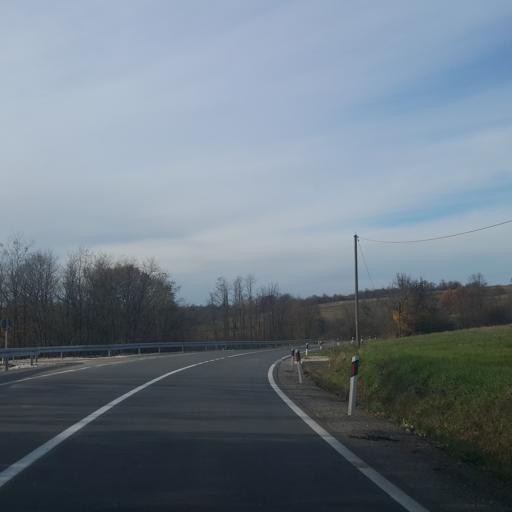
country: RS
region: Central Serbia
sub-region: Sumadijski Okrug
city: Arangelovac
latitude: 44.3405
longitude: 20.4187
